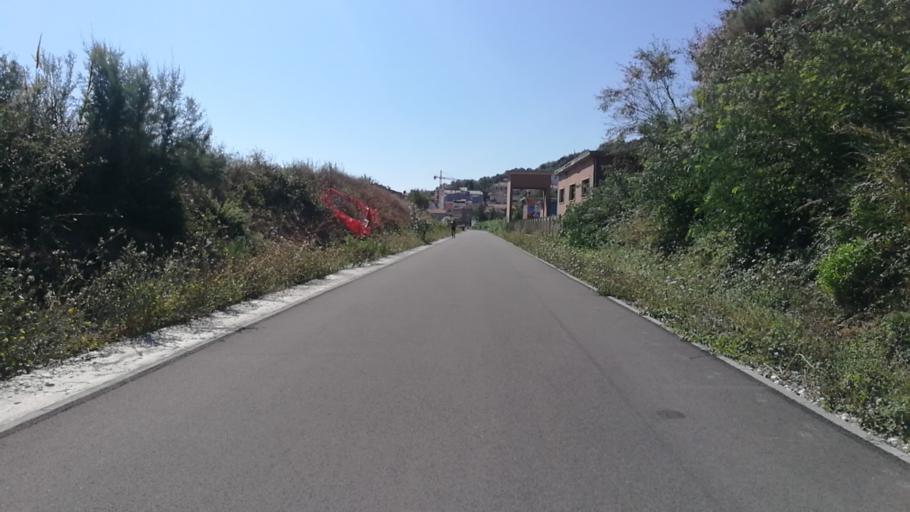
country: IT
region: Abruzzo
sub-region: Provincia di Chieti
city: Marina di San Vito
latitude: 42.3111
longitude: 14.4424
